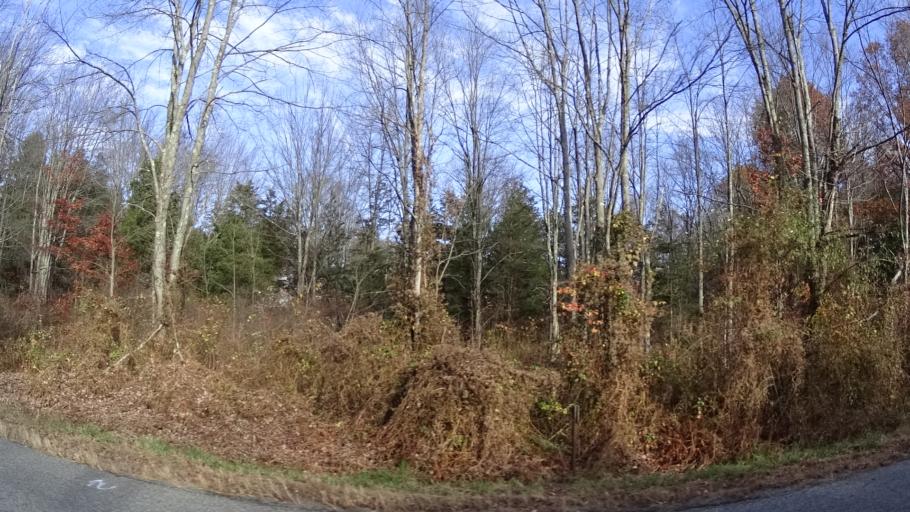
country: US
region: New Jersey
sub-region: Morris County
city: Morristown
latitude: 40.7302
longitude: -74.4964
